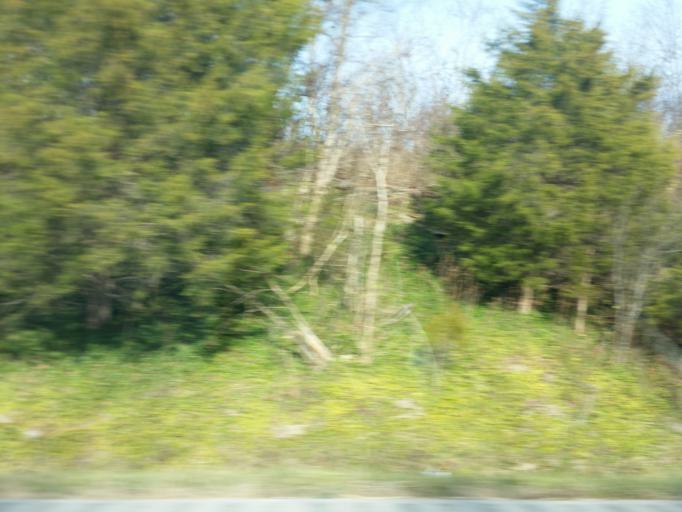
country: US
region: Kentucky
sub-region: Pendleton County
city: Falmouth
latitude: 38.5377
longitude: -84.2828
